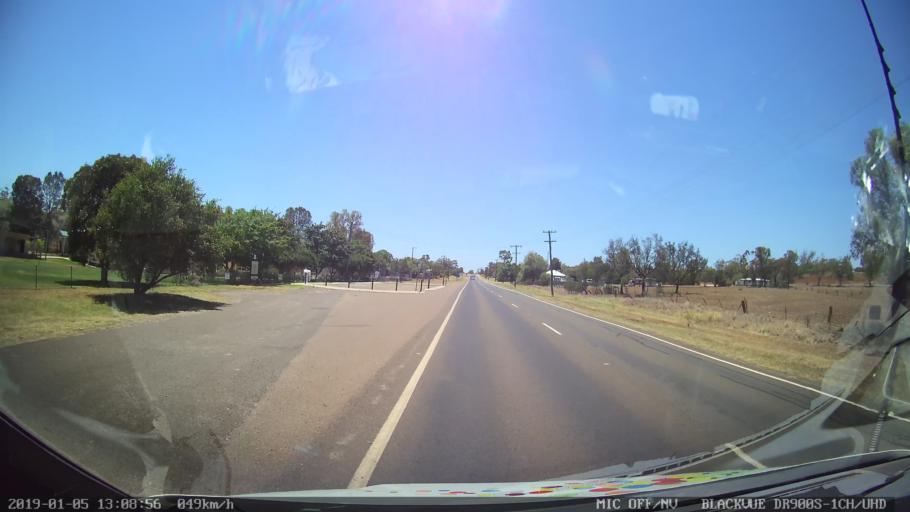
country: AU
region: New South Wales
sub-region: Gunnedah
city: Gunnedah
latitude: -31.0995
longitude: 149.9063
